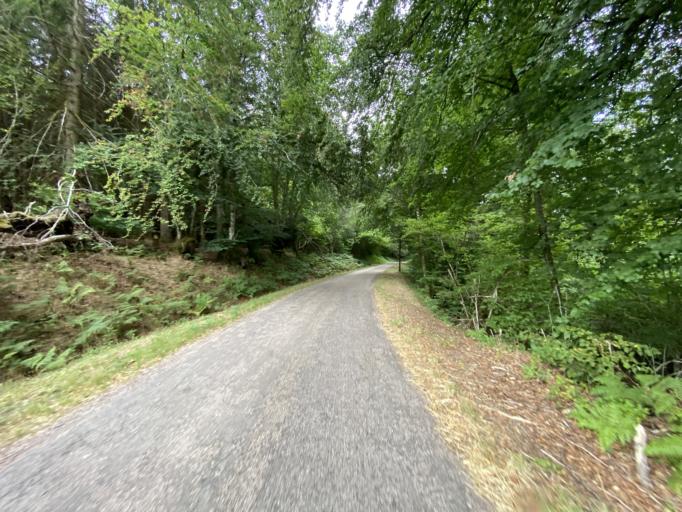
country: FR
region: Bourgogne
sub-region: Departement de la Cote-d'Or
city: Saulieu
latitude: 47.2658
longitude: 4.1344
